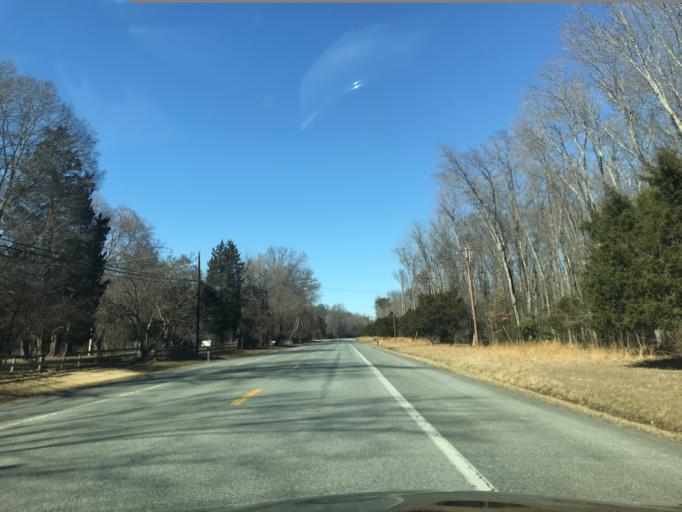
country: US
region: Maryland
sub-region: Charles County
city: Bryans Road
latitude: 38.6704
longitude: -77.0860
